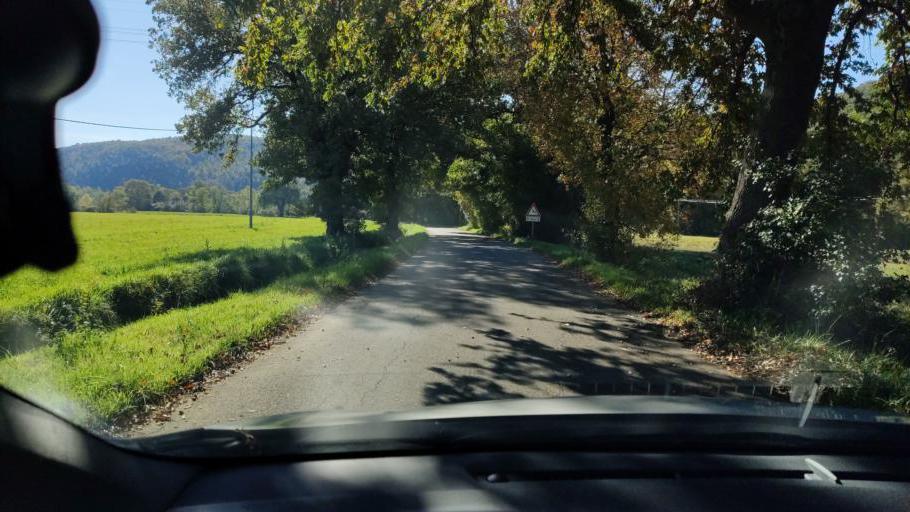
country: IT
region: Umbria
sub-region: Provincia di Terni
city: Amelia
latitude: 42.5934
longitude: 12.4360
